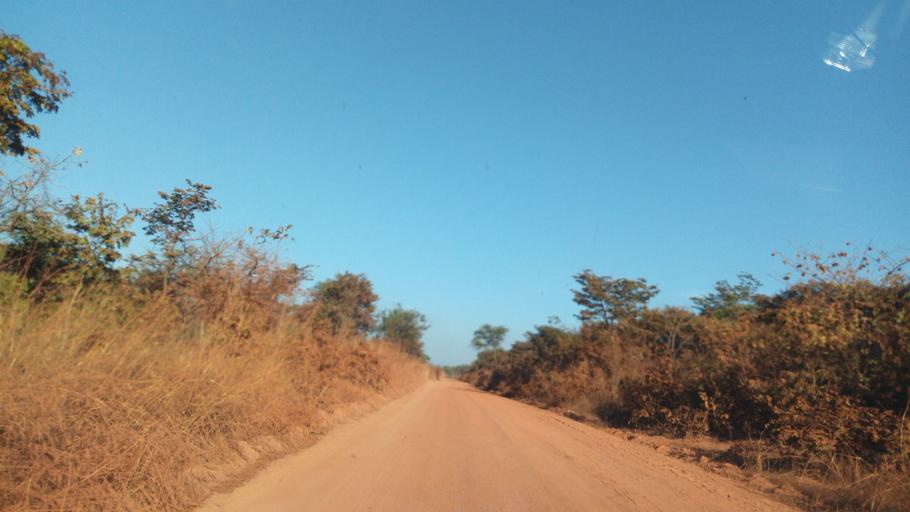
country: ZM
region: Luapula
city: Mwense
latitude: -10.4858
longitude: 28.4939
